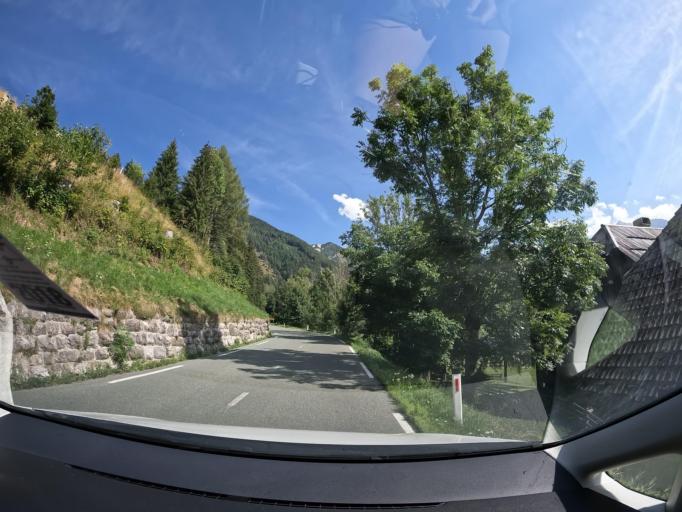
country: AT
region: Carinthia
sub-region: Politischer Bezirk Feldkirchen
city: Glanegg
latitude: 46.7181
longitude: 14.1612
